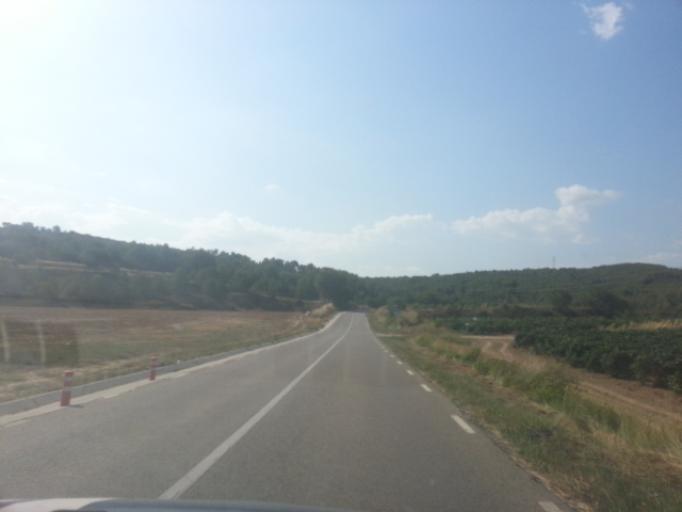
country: ES
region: Catalonia
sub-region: Provincia de Barcelona
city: Avinyonet del Penedes
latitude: 41.3380
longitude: 1.7477
